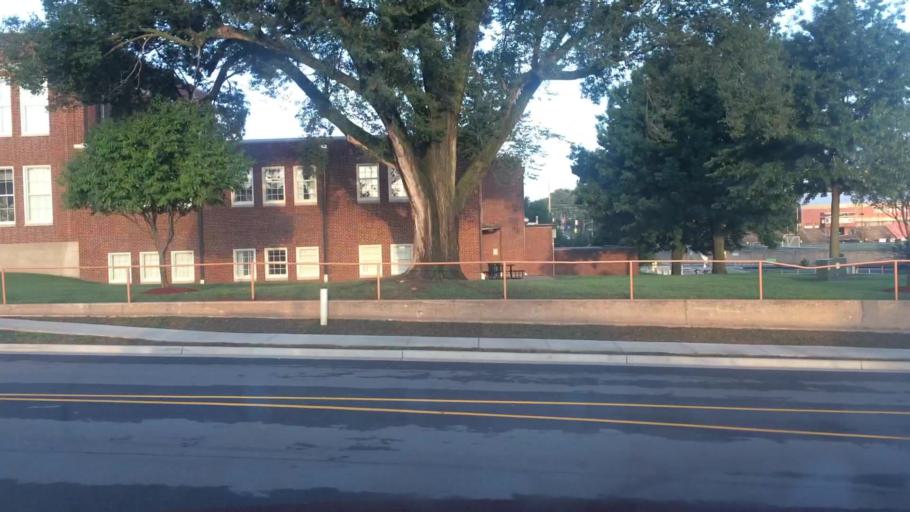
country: US
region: Missouri
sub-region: Greene County
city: Springfield
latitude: 37.2168
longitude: -93.2812
